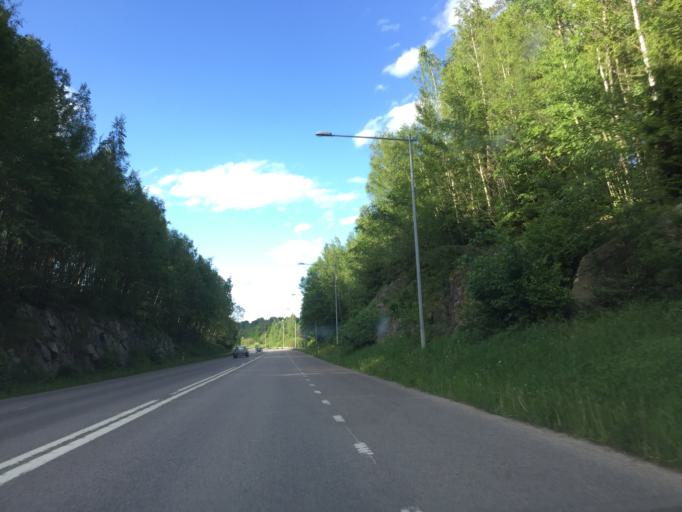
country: SE
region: OErebro
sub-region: Orebro Kommun
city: Orebro
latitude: 59.2479
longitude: 15.2375
